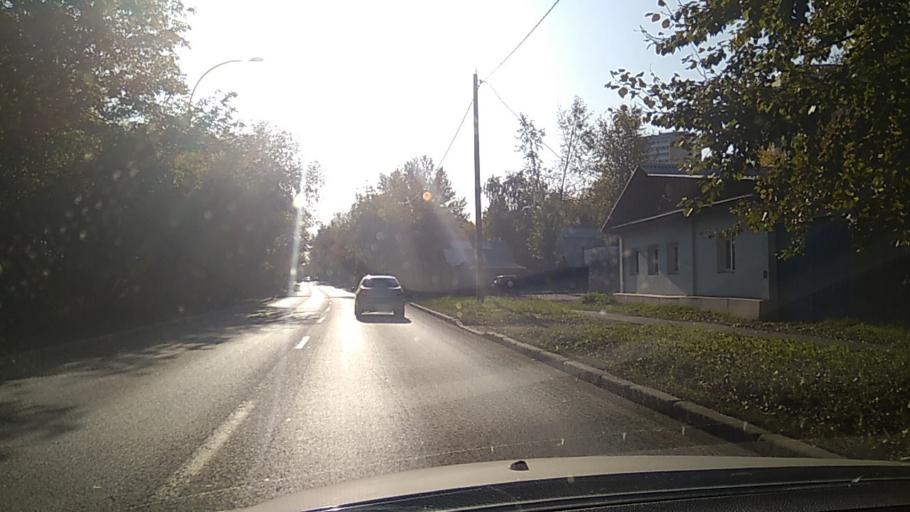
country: RU
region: Sverdlovsk
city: Yekaterinburg
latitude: 56.7783
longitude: 60.6428
